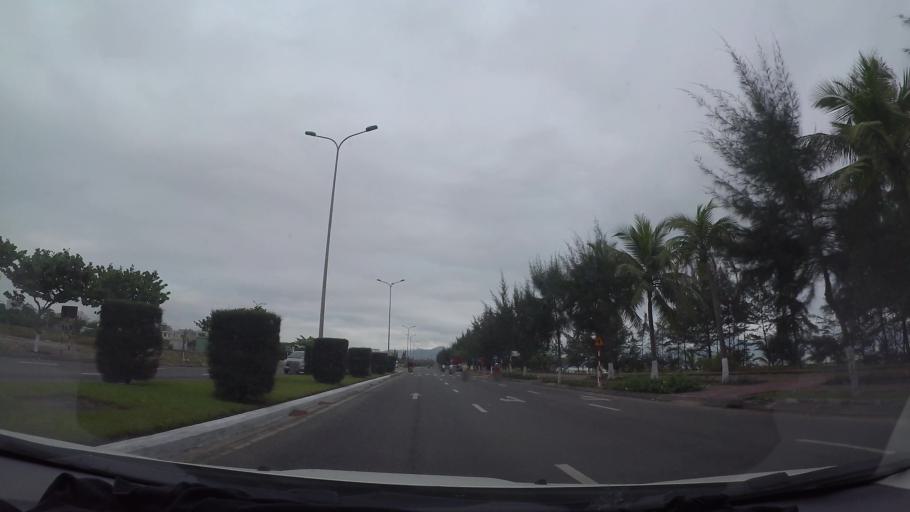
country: VN
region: Da Nang
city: Lien Chieu
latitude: 16.0902
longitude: 108.1522
